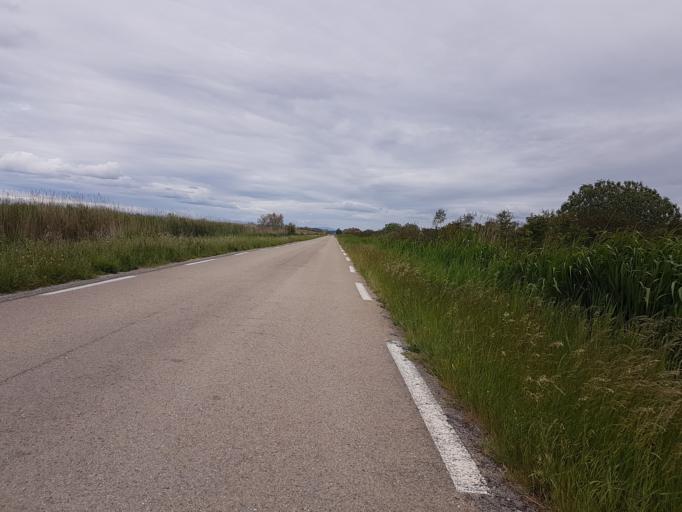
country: FR
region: Languedoc-Roussillon
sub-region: Departement du Gard
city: Vauvert
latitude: 43.6158
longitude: 4.3249
